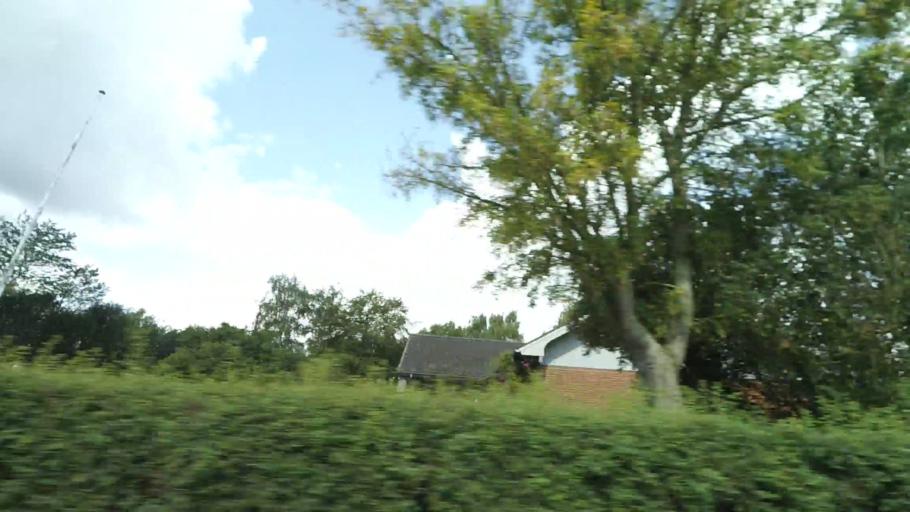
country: DK
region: Central Jutland
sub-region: Norddjurs Kommune
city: Allingabro
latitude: 56.5009
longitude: 10.3738
